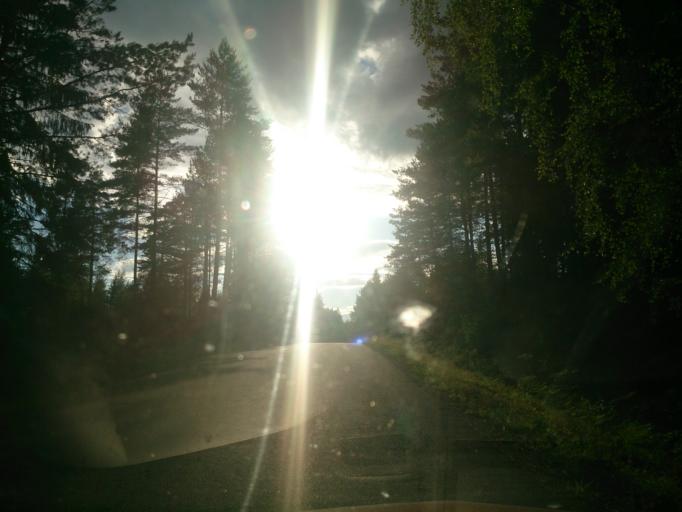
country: SE
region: OEstergoetland
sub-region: Norrkopings Kommun
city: Jursla
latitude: 58.7248
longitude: 16.1239
